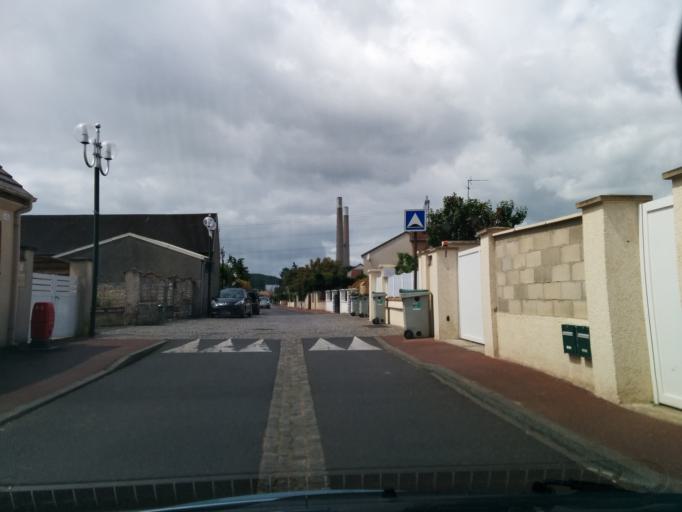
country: FR
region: Ile-de-France
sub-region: Departement des Yvelines
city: Porcheville
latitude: 48.9702
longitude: 1.7769
